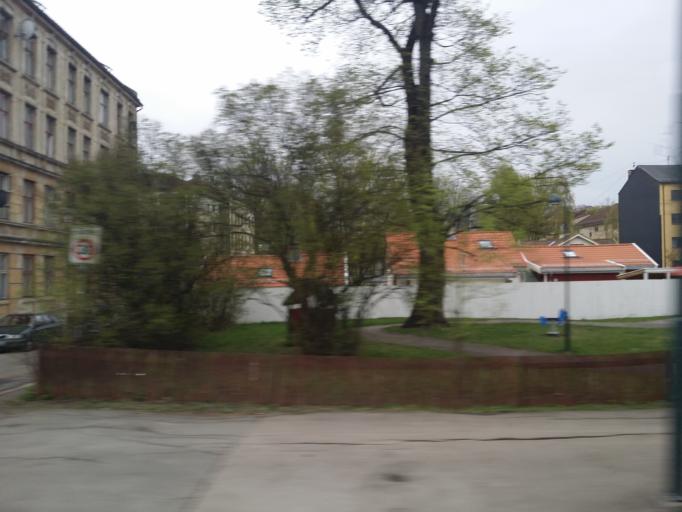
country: NO
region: Oslo
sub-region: Oslo
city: Oslo
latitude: 59.9084
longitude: 10.7843
